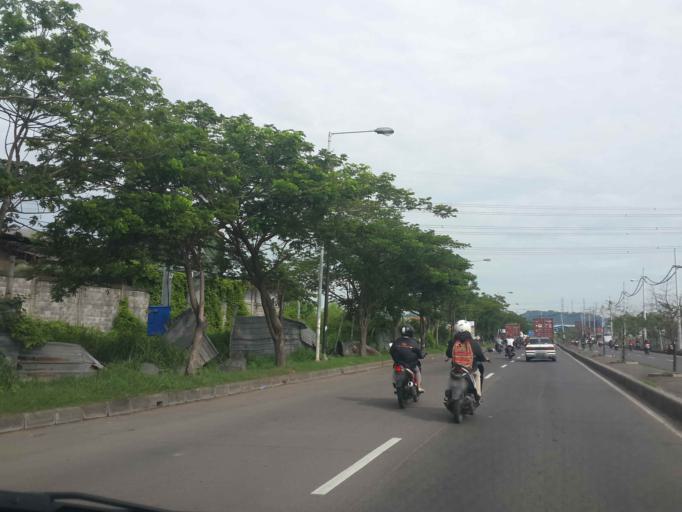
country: ID
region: East Java
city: Kebomas
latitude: -7.2013
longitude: 112.6490
